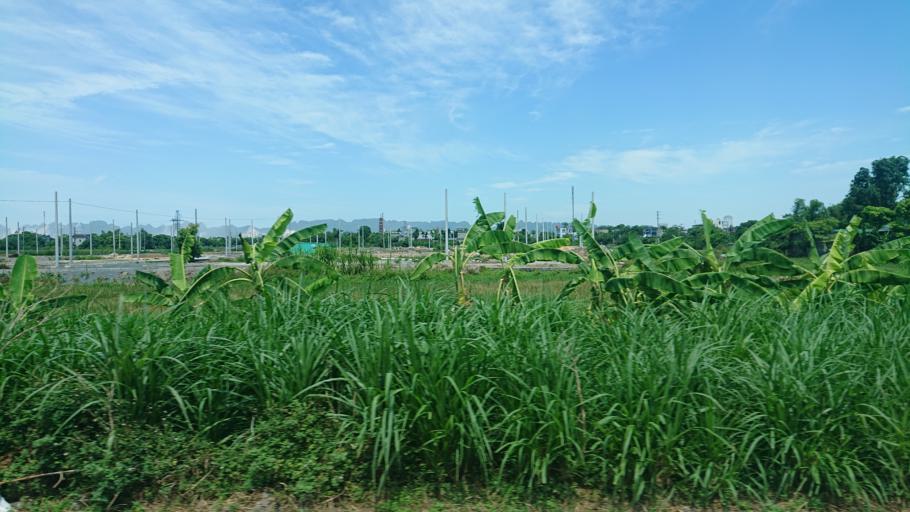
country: VN
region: Ha Nam
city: Thanh Pho Phu Ly
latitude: 20.5347
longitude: 105.9454
